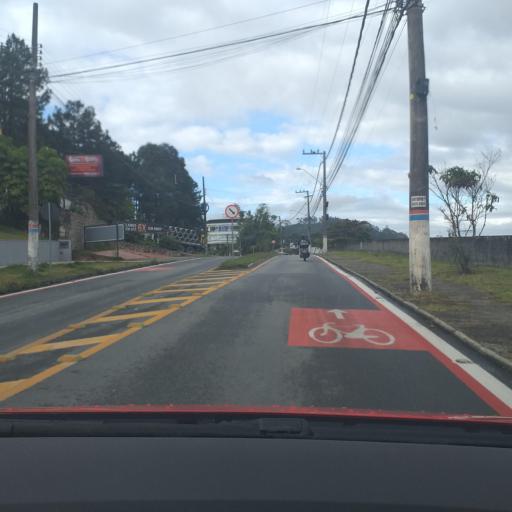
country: BR
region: Santa Catarina
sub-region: Florianopolis
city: Corrego Grande
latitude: -27.5955
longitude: -48.4977
